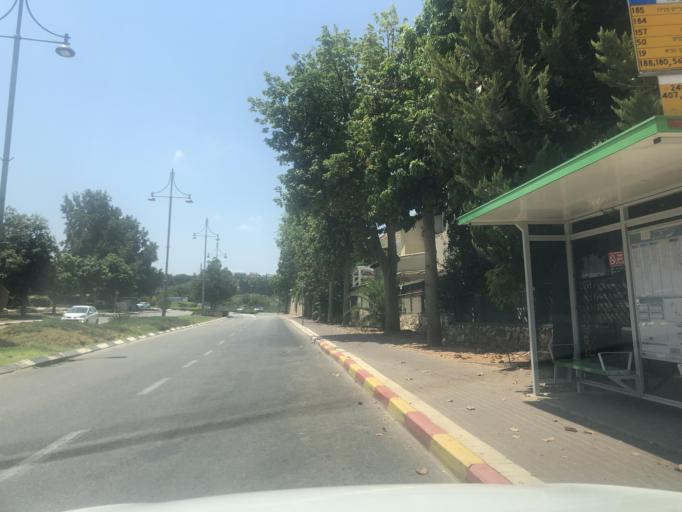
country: IL
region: Haifa
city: Daliyat el Karmil
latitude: 32.6384
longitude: 35.0850
